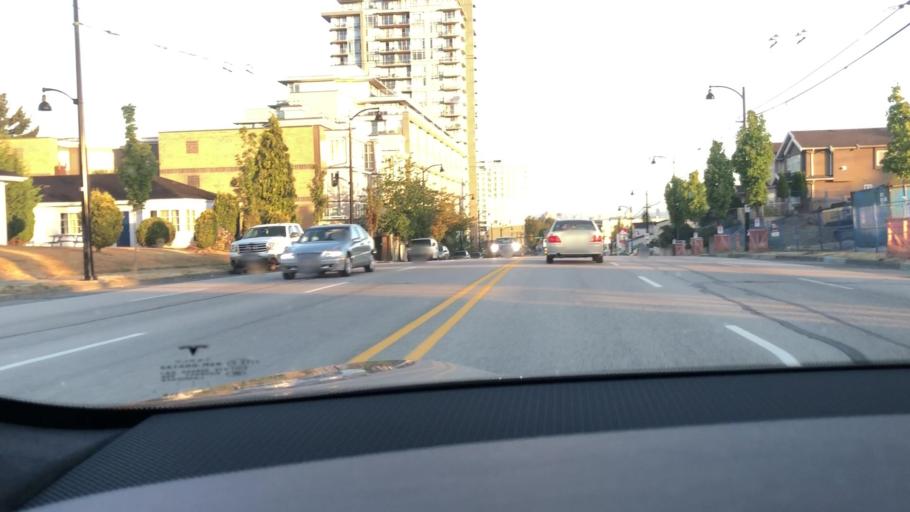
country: CA
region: British Columbia
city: Vancouver
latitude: 49.2409
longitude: -123.0557
